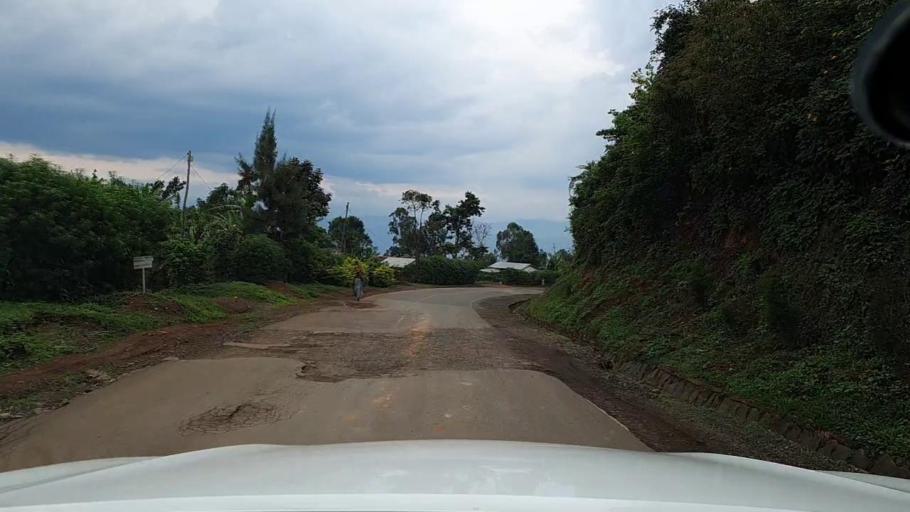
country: RW
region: Western Province
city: Cyangugu
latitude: -2.6517
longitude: 28.9680
